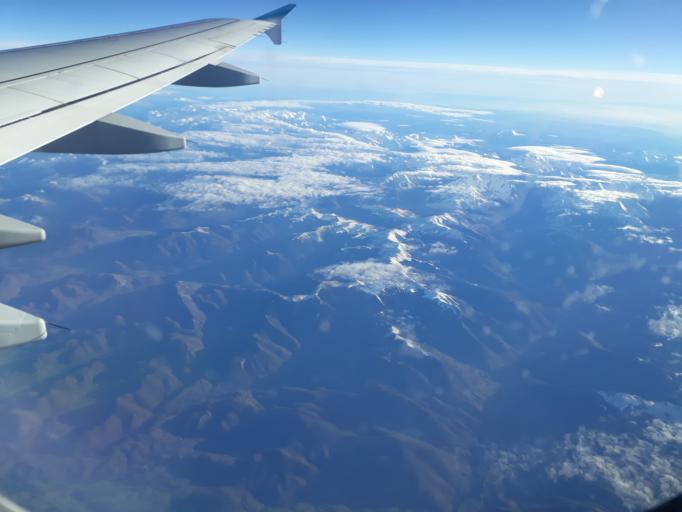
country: FR
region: Midi-Pyrenees
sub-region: Departement des Hautes-Pyrenees
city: Lannemezan
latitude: 43.1232
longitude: 0.3584
